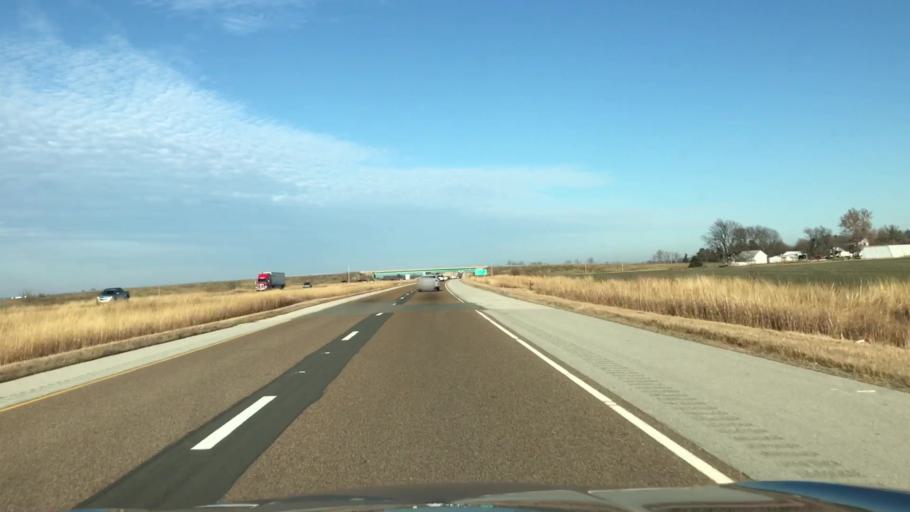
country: US
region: Illinois
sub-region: Montgomery County
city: Litchfield
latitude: 39.1859
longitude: -89.6738
